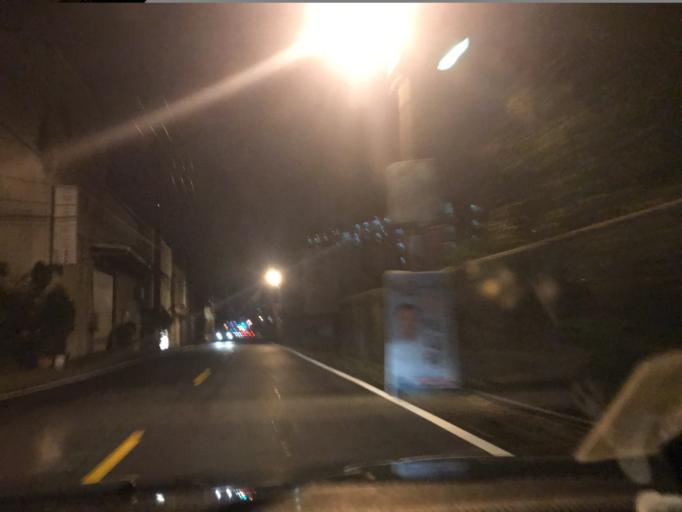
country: TW
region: Taiwan
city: Taoyuan City
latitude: 24.9444
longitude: 121.2343
